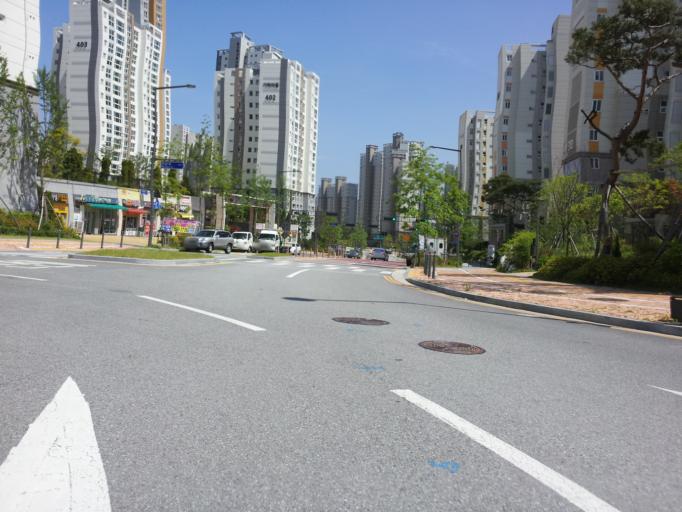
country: KR
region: Chungcheongnam-do
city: Gongju
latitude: 36.5074
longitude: 127.2357
